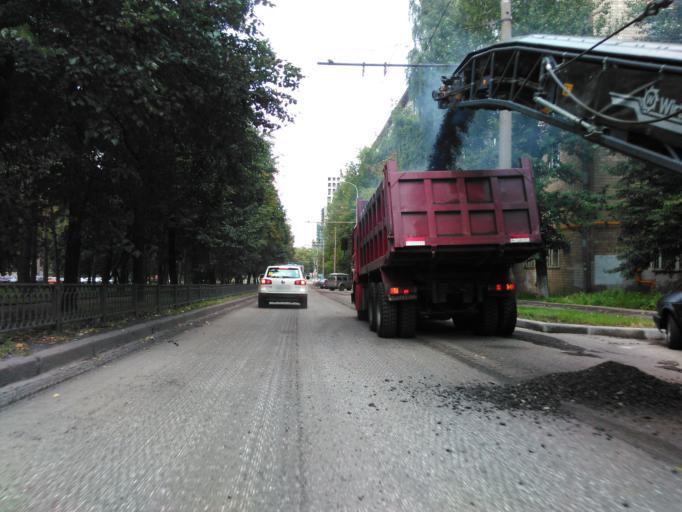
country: RU
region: Moskovskaya
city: Semenovskoye
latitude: 55.6826
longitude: 37.5223
